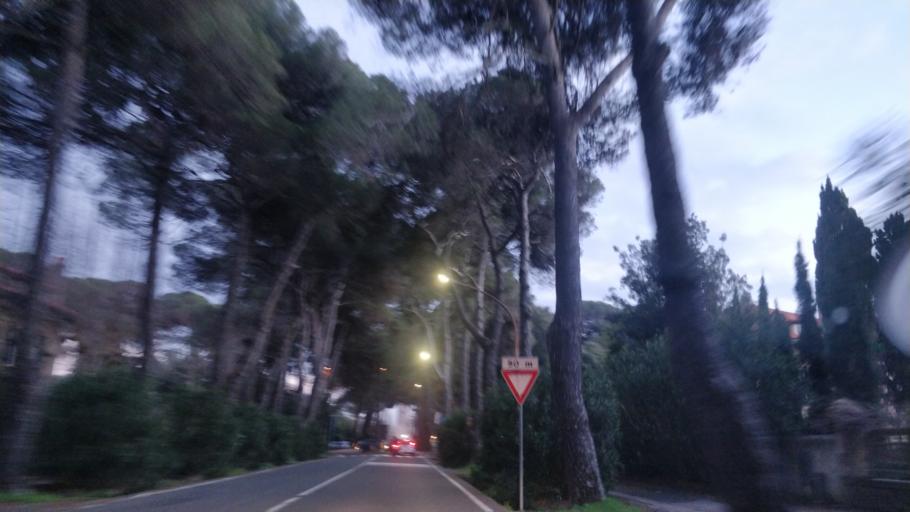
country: IT
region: Tuscany
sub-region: Provincia di Livorno
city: Rosignano Solvay-Castiglioncello
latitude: 43.3889
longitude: 10.4419
